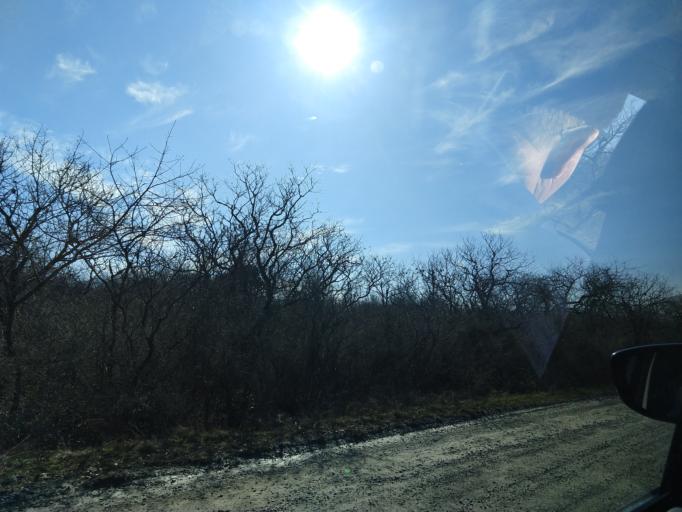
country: US
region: Massachusetts
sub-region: Essex County
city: Ipswich
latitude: 42.7416
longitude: -70.7943
